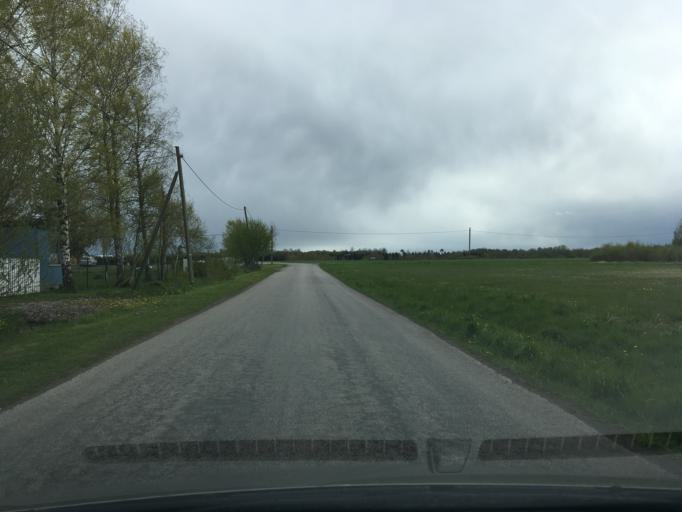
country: EE
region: Harju
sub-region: Joelaehtme vald
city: Loo
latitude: 59.3891
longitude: 24.9612
